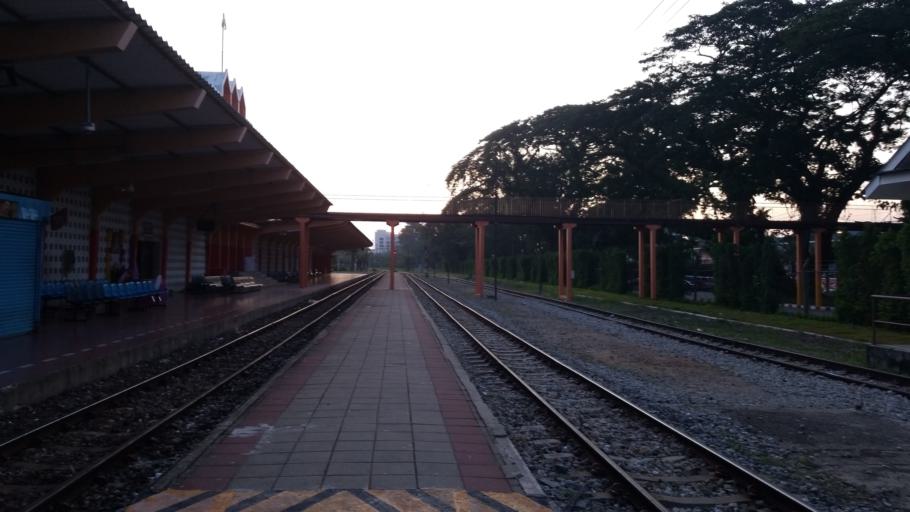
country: TH
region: Narathiwat
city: Su-ngai Kolok
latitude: 6.0257
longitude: 101.9646
